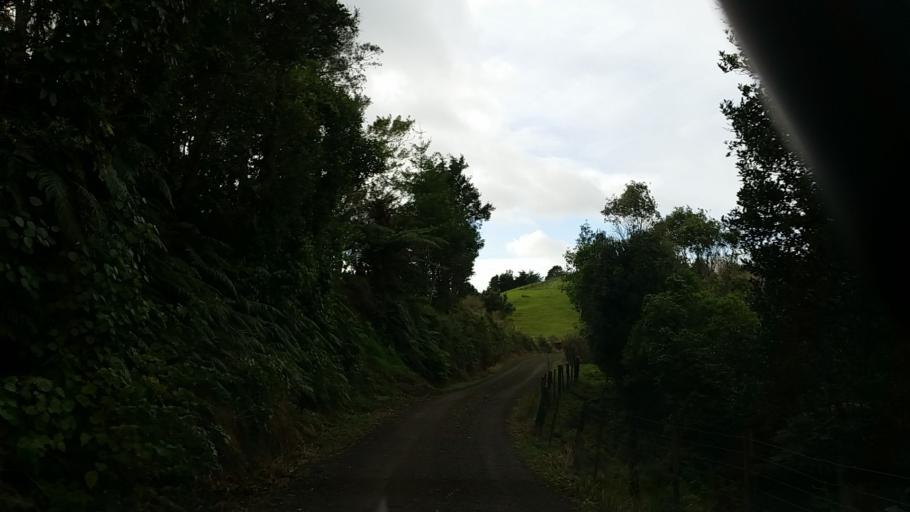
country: NZ
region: Taranaki
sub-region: New Plymouth District
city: Waitara
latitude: -39.0688
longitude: 174.3970
